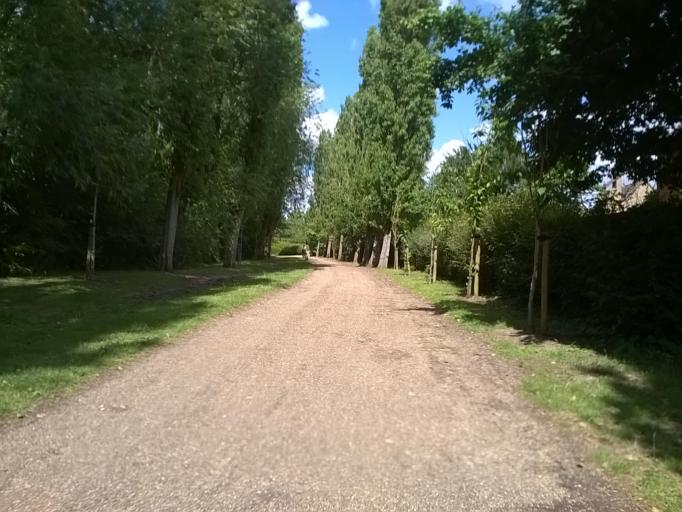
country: GB
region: England
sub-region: Milton Keynes
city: Milton Keynes
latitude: 52.0628
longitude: -0.7394
